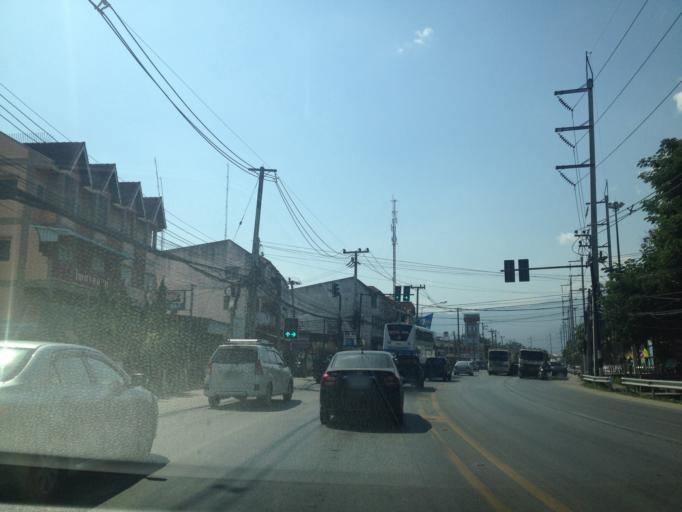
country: TH
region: Chiang Mai
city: Chom Thong
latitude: 18.4178
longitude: 98.6774
